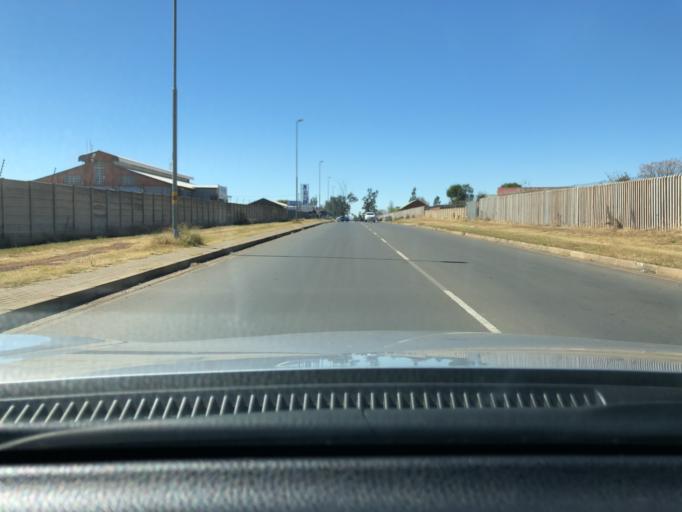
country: ZA
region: KwaZulu-Natal
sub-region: Amajuba District Municipality
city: Newcastle
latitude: -27.7603
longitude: 29.9487
